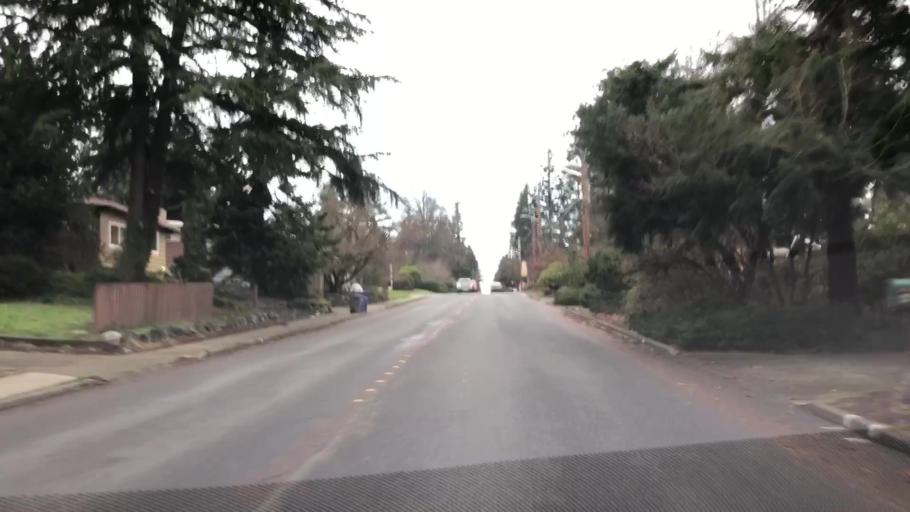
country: US
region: Washington
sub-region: King County
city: West Lake Sammamish
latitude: 47.6100
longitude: -122.1213
